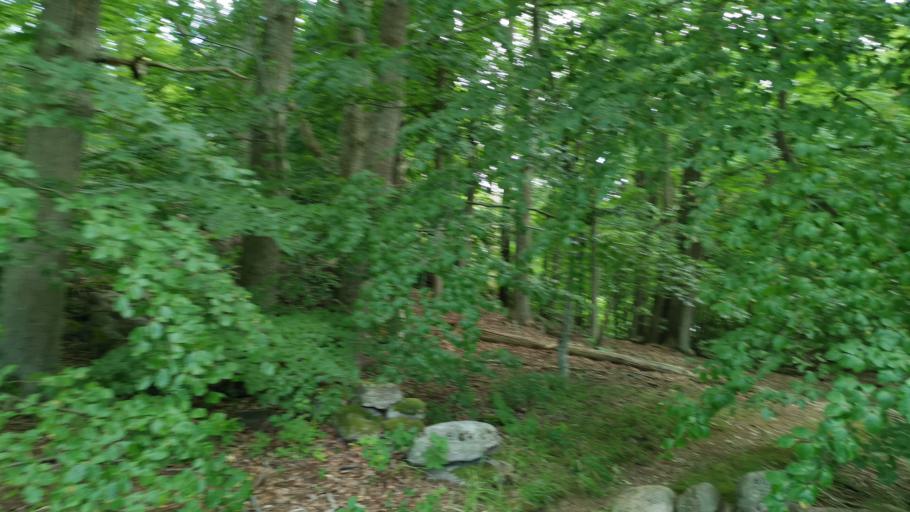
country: SE
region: Vaestra Goetaland
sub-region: Lysekils Kommun
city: Lysekil
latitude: 58.2427
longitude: 11.4893
